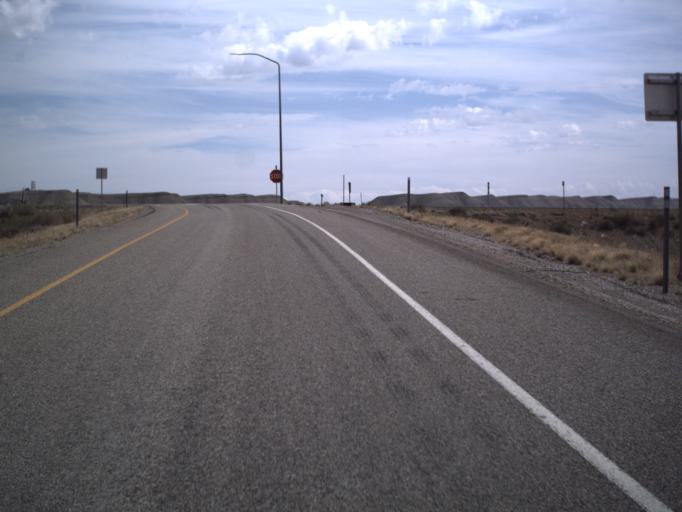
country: US
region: Utah
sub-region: Carbon County
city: East Carbon City
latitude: 38.9757
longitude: -110.1229
